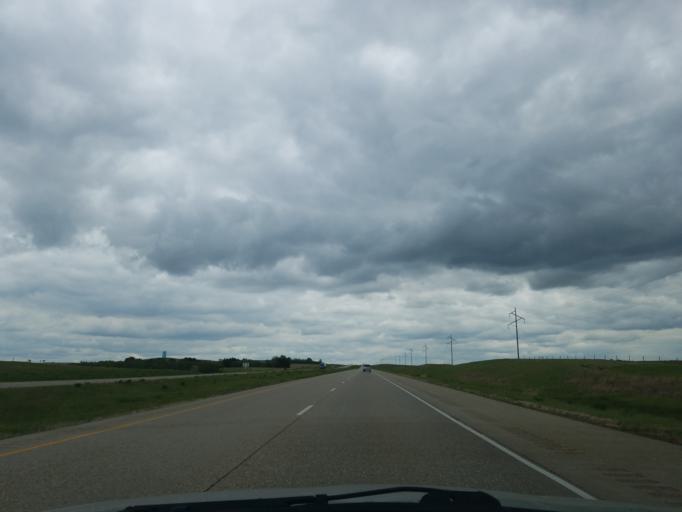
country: US
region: North Dakota
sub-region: Morton County
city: Mandan
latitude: 46.8623
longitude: -101.1308
